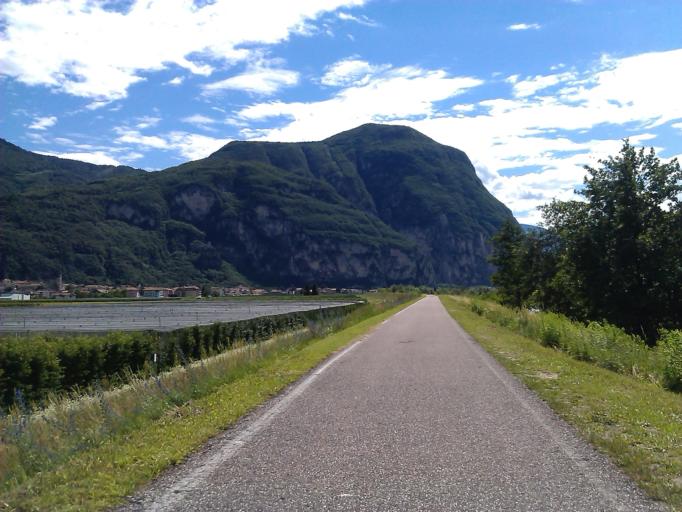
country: IT
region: Trentino-Alto Adige
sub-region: Bolzano
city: Salorno
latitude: 46.2523
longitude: 11.2174
